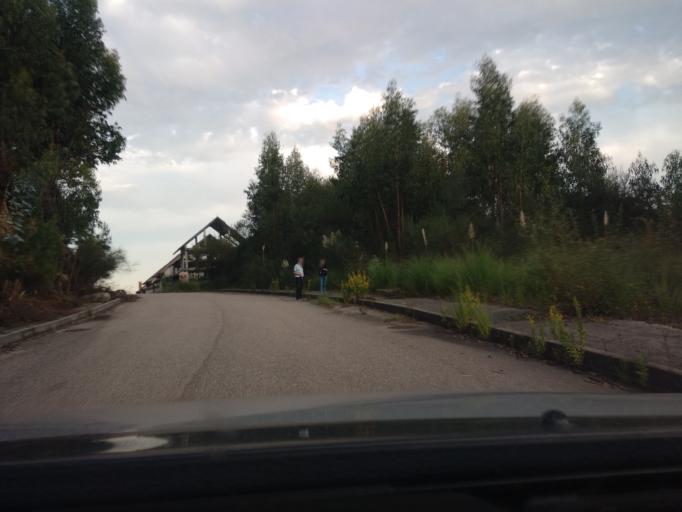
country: ES
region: Galicia
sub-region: Provincia de Pontevedra
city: Moana
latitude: 42.2976
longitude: -8.6911
